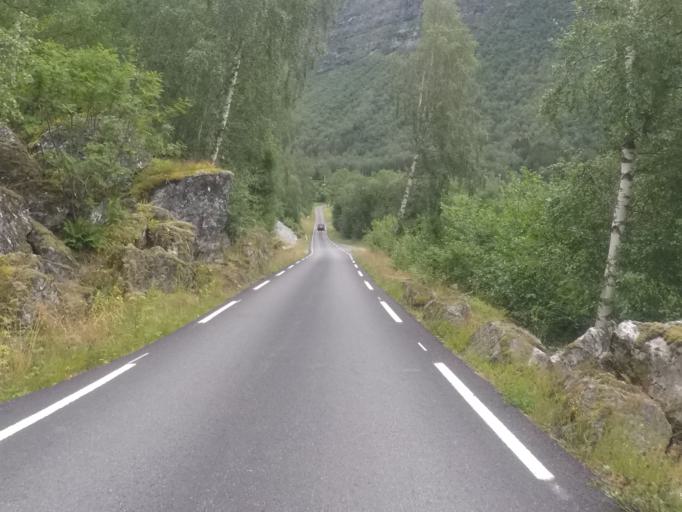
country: NO
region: Sogn og Fjordane
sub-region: Stryn
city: Stryn
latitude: 61.8038
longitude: 7.0062
